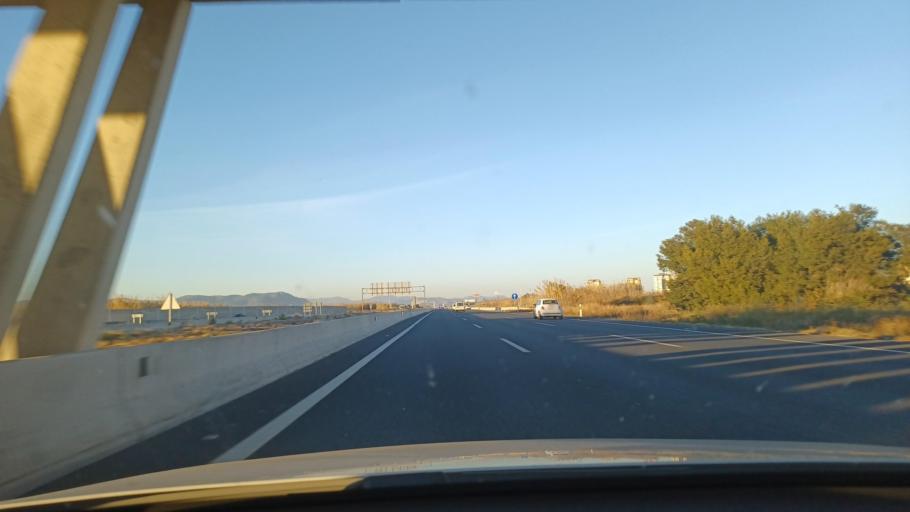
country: ES
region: Valencia
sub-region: Provincia de Valencia
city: Albuixech
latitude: 39.5517
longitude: -0.2975
